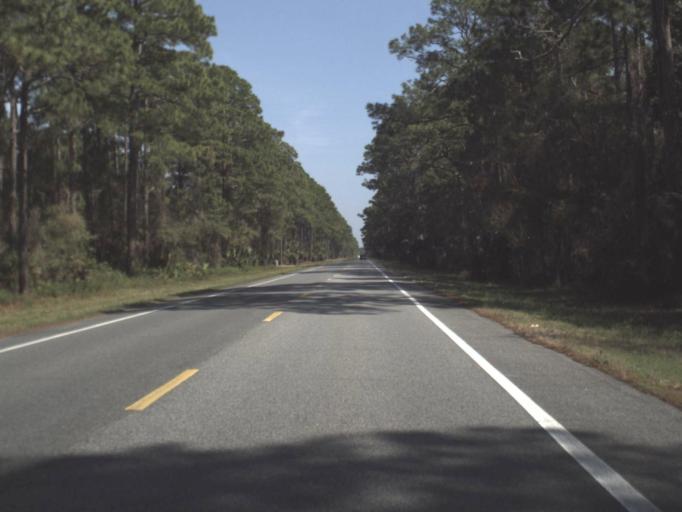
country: US
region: Florida
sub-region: Franklin County
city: Apalachicola
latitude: 29.7166
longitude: -85.0439
